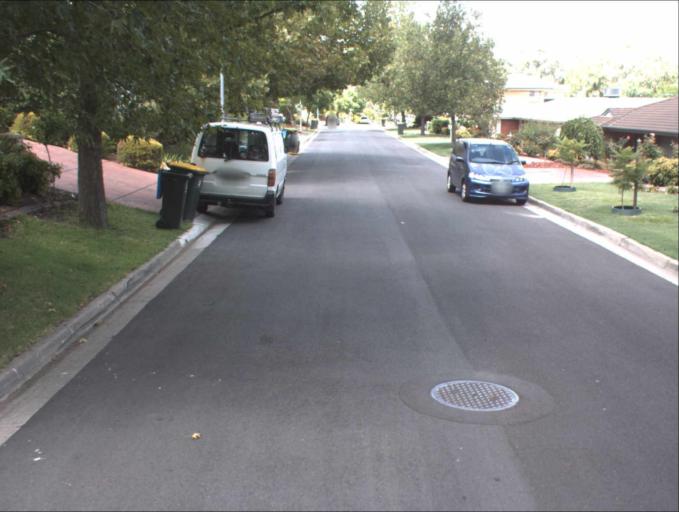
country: AU
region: South Australia
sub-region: Campbelltown
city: Paradise
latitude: -34.8652
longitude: 138.6682
